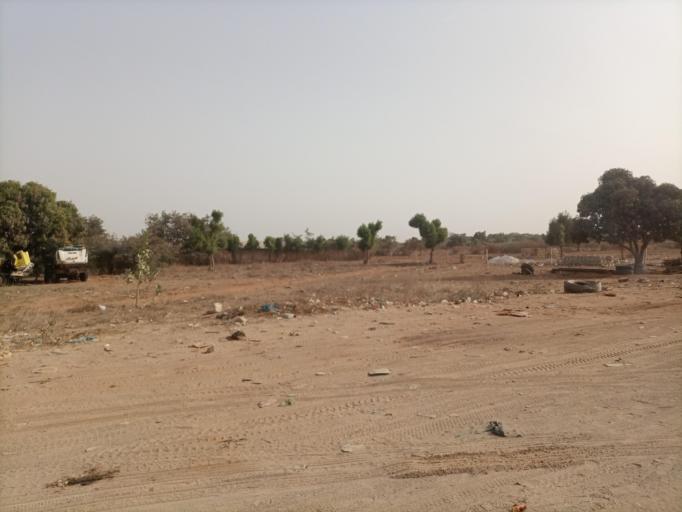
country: SN
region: Thies
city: Nguekhokh
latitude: 14.5855
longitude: -17.0281
